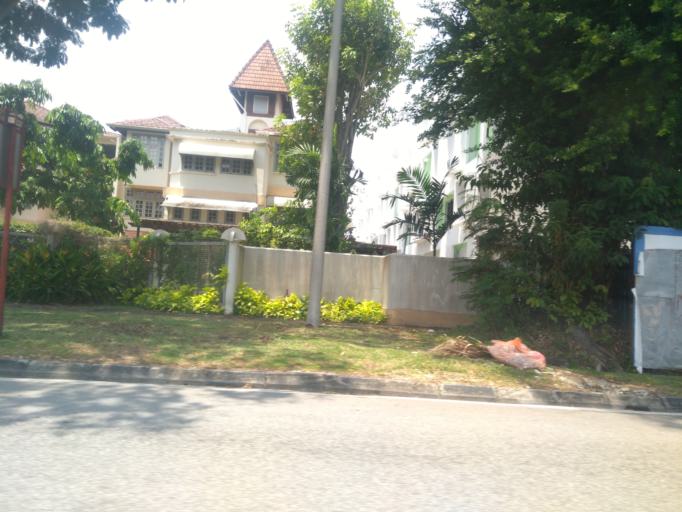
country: MY
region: Penang
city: George Town
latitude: 5.4272
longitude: 100.3101
